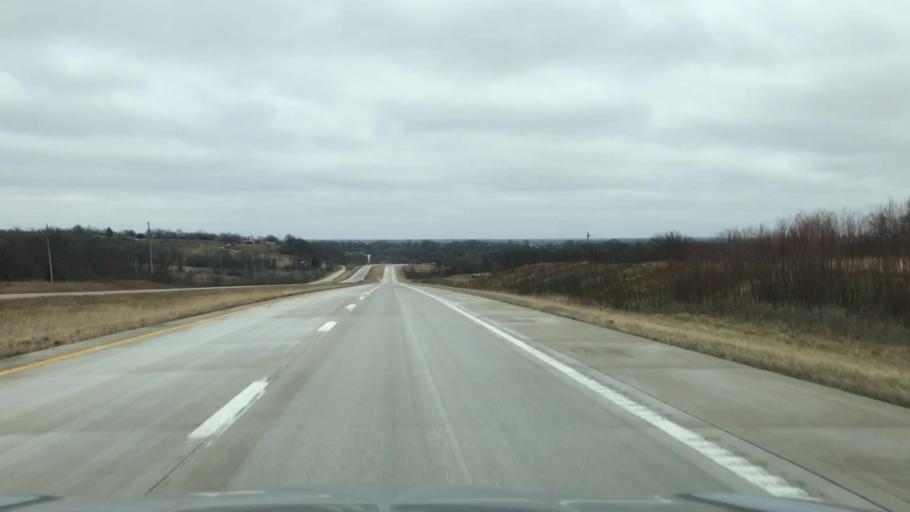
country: US
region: Missouri
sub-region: Livingston County
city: Chillicothe
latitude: 39.7395
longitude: -93.6556
